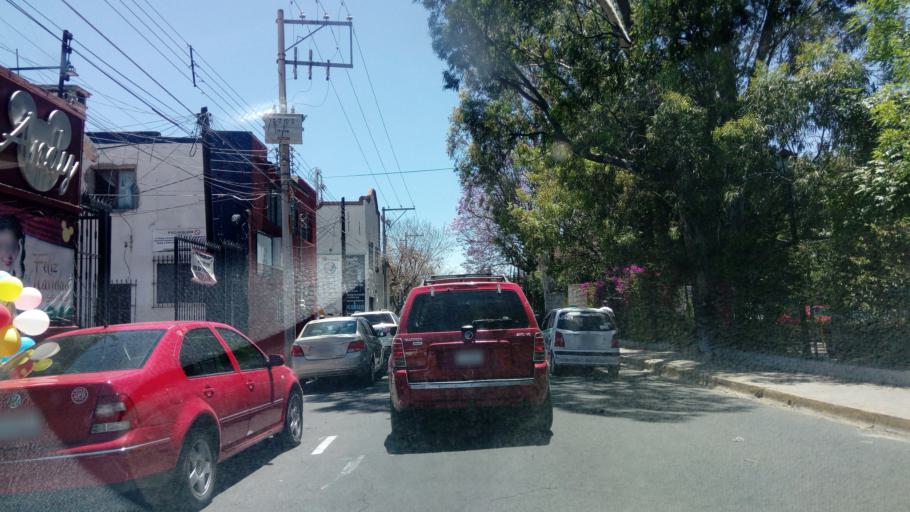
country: MX
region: Durango
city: Victoria de Durango
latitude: 24.0273
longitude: -104.6614
